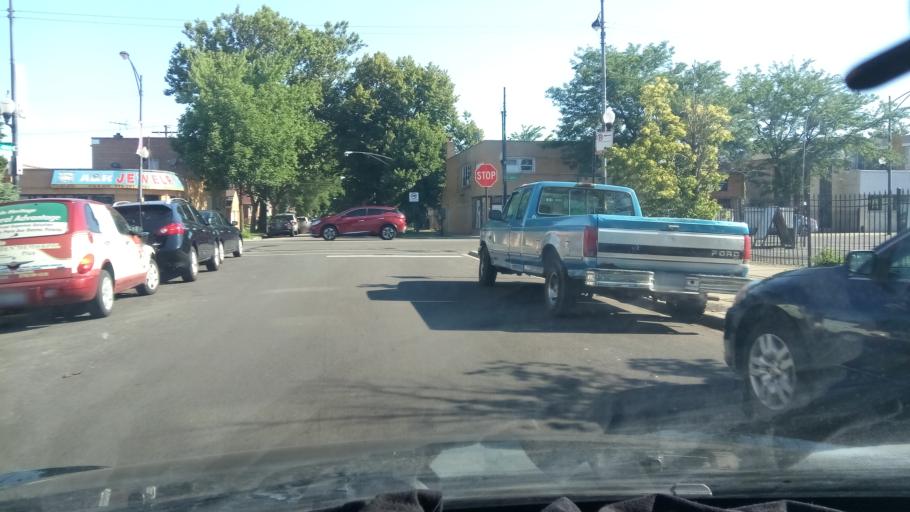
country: US
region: Illinois
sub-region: Cook County
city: Hometown
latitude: 41.7777
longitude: -87.7263
